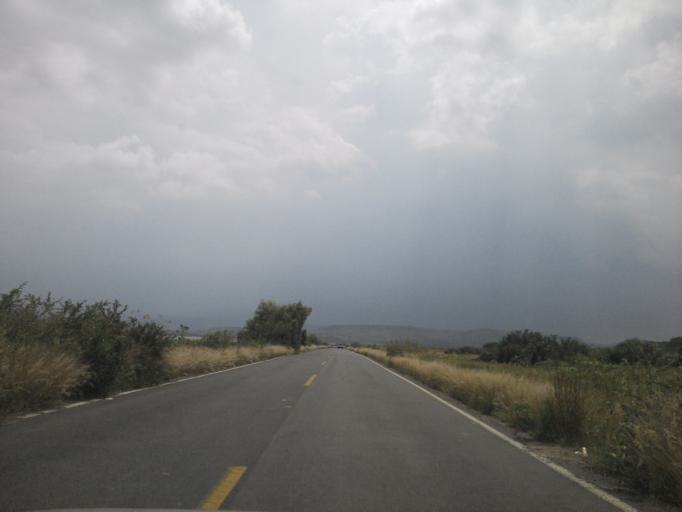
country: MX
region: Jalisco
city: San Diego de Alejandria
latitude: 20.9001
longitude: -102.0033
